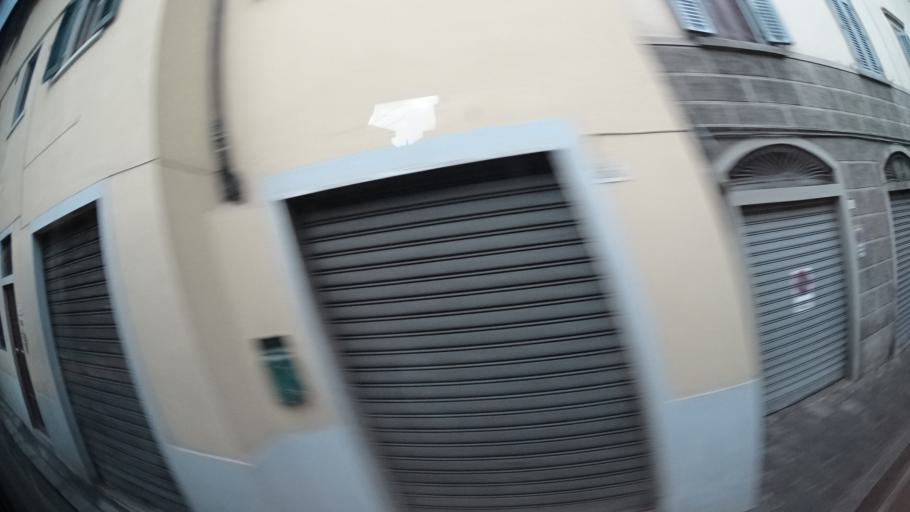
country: IT
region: Tuscany
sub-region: Province of Florence
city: Florence
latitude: 43.7575
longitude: 11.2404
